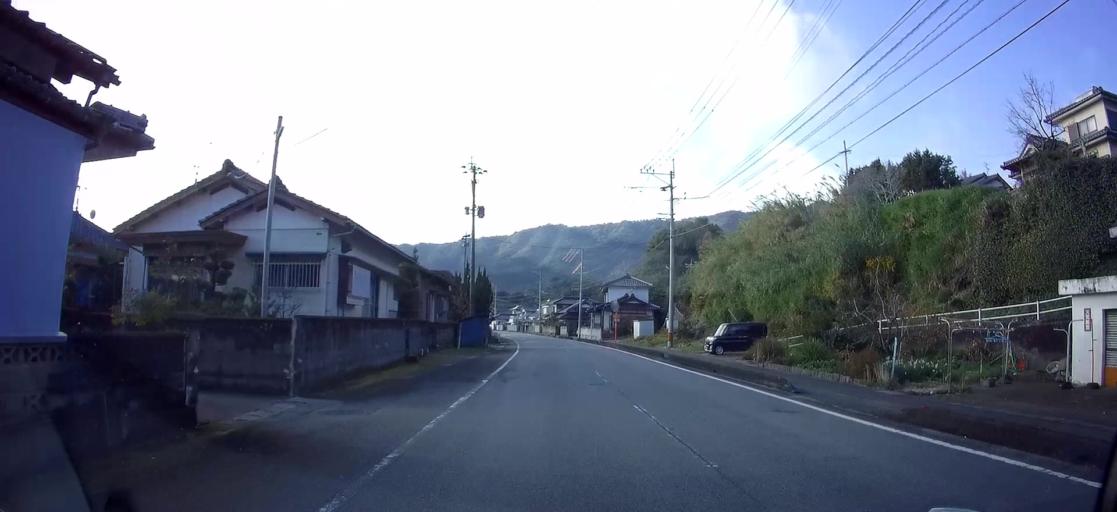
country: JP
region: Kumamoto
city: Minamata
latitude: 32.3900
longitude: 130.3751
